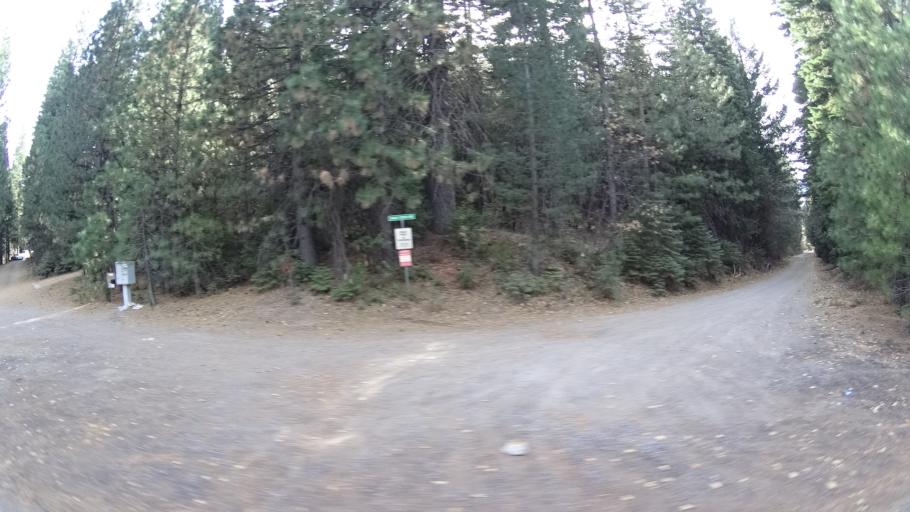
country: US
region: California
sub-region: Siskiyou County
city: Weed
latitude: 41.3820
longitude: -122.3893
